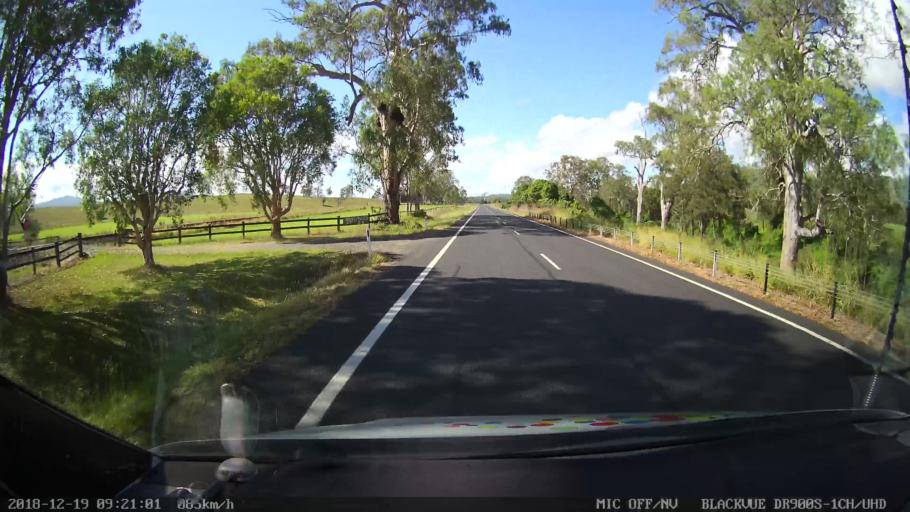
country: AU
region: New South Wales
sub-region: Kyogle
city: Kyogle
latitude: -28.5785
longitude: 152.9825
